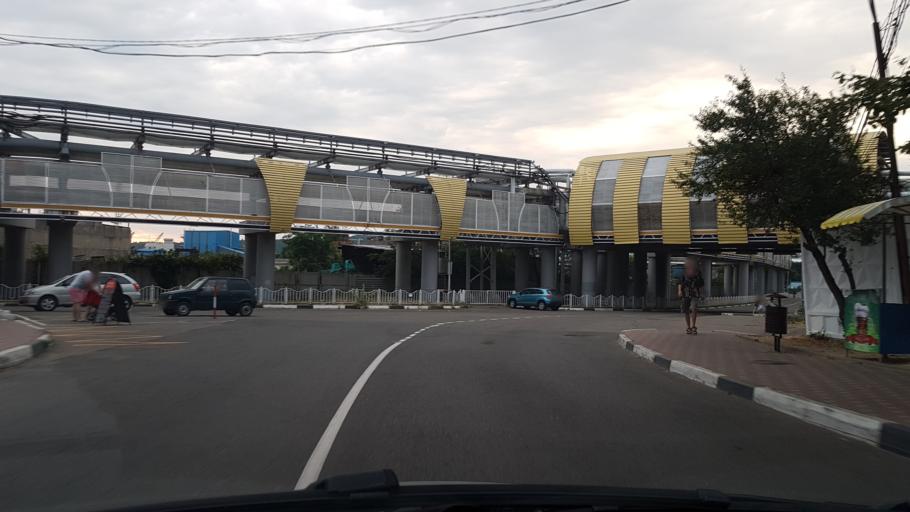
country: RU
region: Krasnodarskiy
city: Tuapse
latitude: 44.0905
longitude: 39.0817
